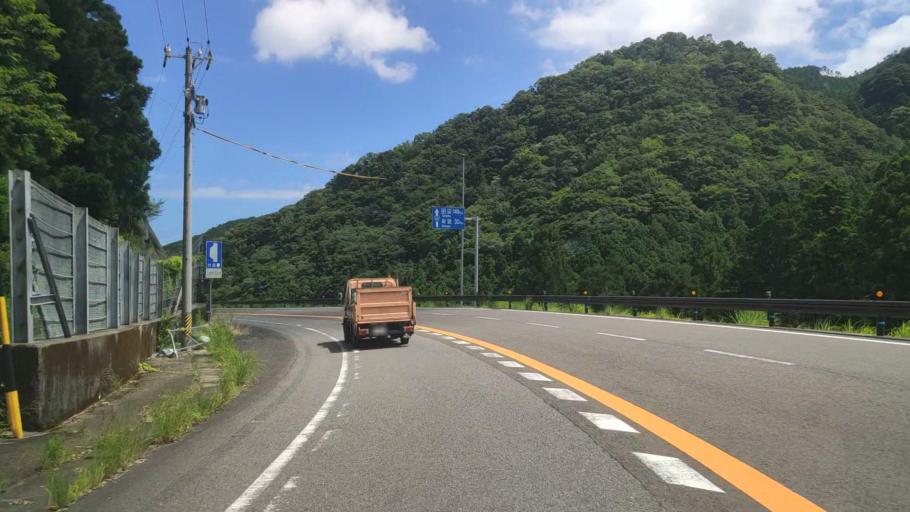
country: JP
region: Mie
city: Owase
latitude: 33.9219
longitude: 136.0965
